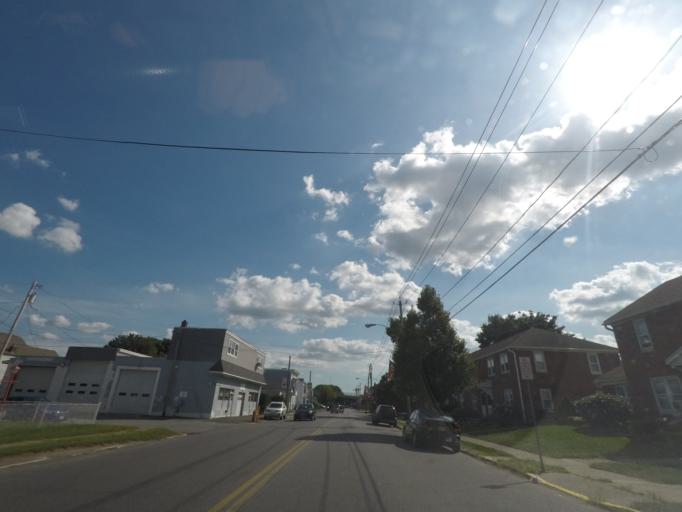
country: US
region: New York
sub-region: Albany County
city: Watervliet
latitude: 42.7318
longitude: -73.6998
